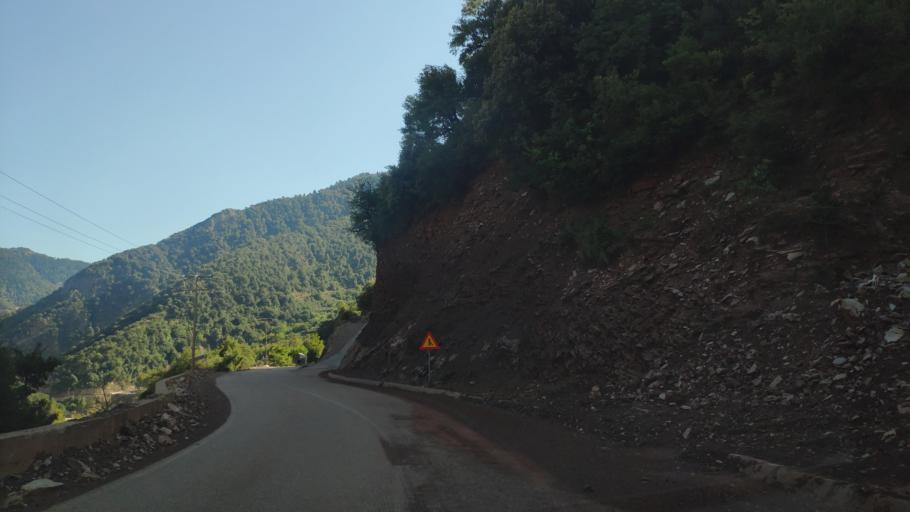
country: GR
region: Central Greece
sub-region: Nomos Evrytanias
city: Kerasochori
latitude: 39.0833
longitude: 21.5966
